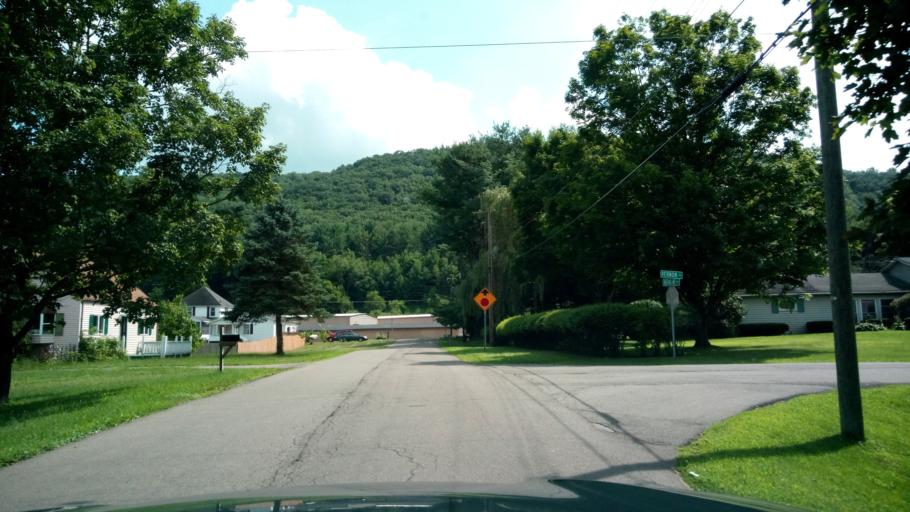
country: US
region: New York
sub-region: Chemung County
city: West Elmira
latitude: 42.0827
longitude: -76.8748
